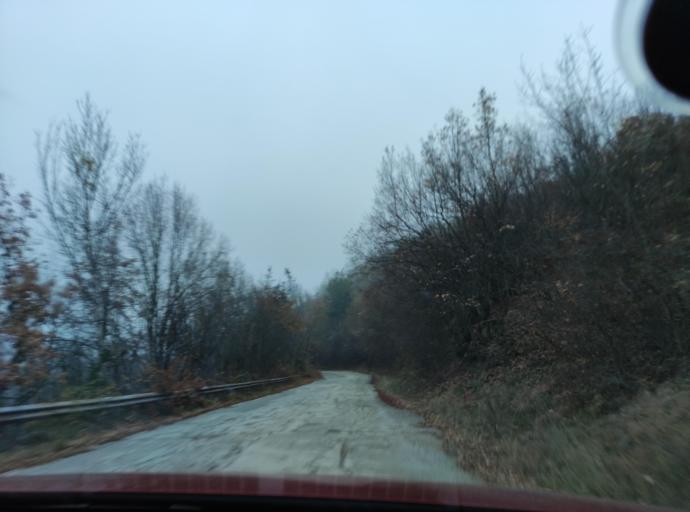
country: BG
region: Lovech
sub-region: Obshtina Yablanitsa
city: Yablanitsa
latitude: 43.1032
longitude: 24.0710
